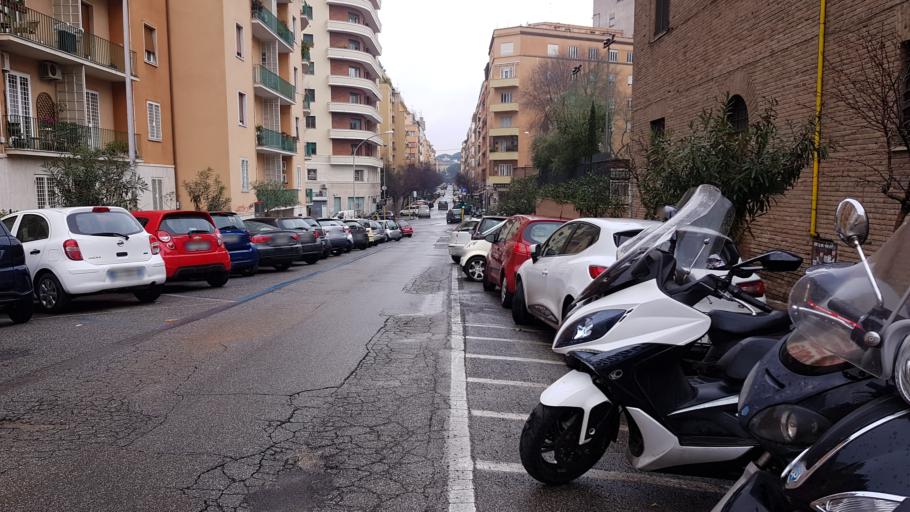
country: IT
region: Latium
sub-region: Citta metropolitana di Roma Capitale
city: Rome
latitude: 41.9103
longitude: 12.5221
